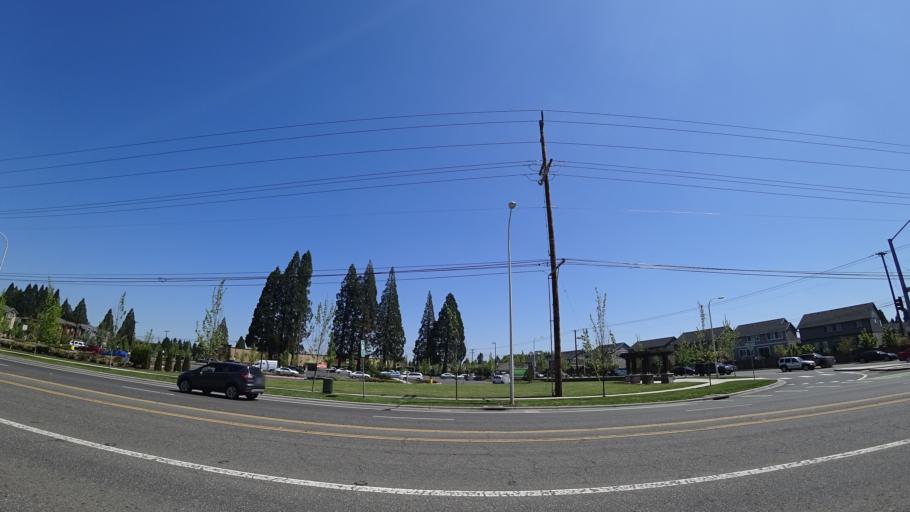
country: US
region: Oregon
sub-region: Washington County
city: Aloha
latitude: 45.5158
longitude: -122.9007
